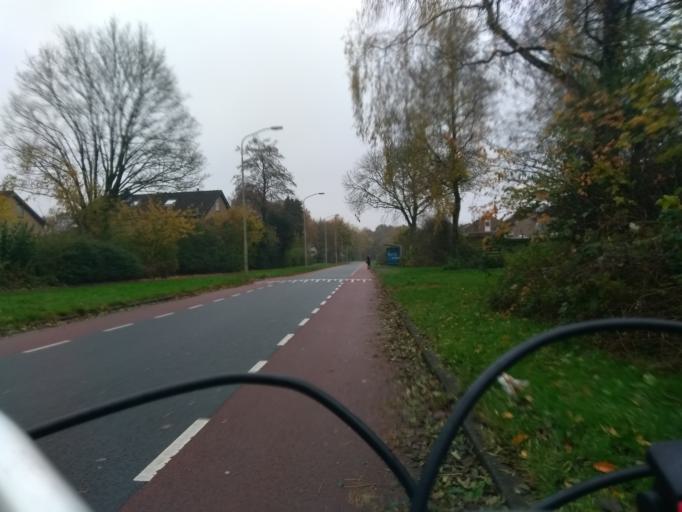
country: NL
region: Drenthe
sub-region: Gemeente Assen
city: Assen
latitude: 53.0096
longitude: 6.5600
